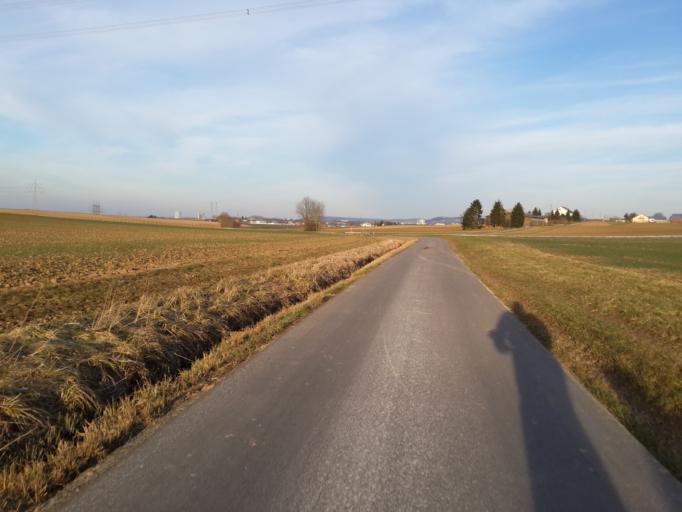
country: DE
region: Baden-Wuerttemberg
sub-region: Regierungsbezirk Stuttgart
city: Nordheim
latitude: 49.1321
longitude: 9.1428
